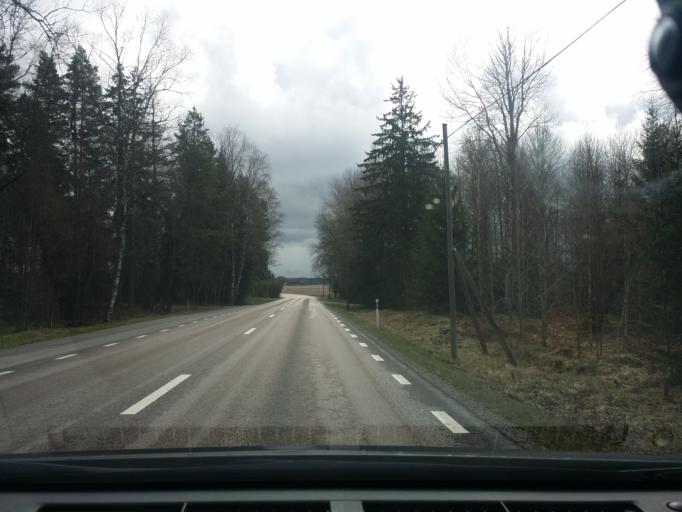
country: SE
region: Uppsala
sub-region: Enkopings Kommun
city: Irsta
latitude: 59.7840
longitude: 16.8395
